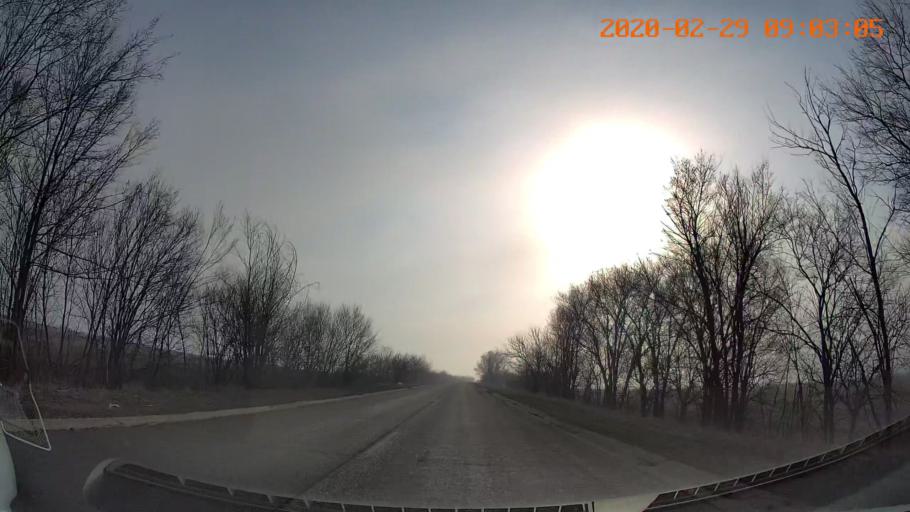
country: UA
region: Odessa
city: Velykoploske
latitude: 46.9179
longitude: 29.7221
